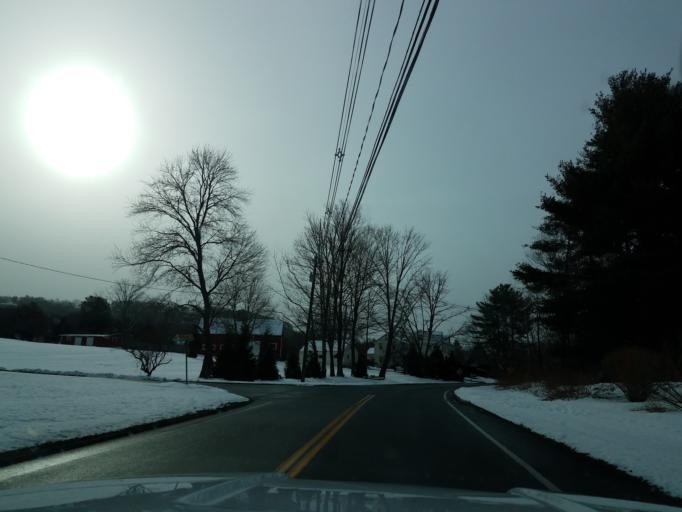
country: US
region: Connecticut
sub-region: Hartford County
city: Farmington
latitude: 41.7600
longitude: -72.8162
